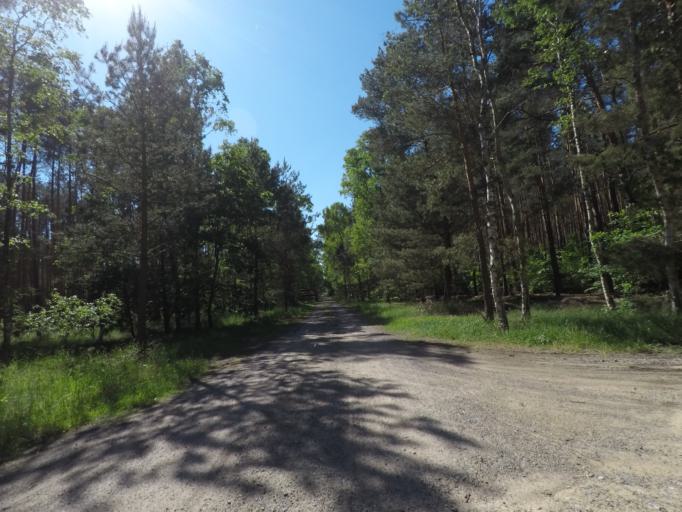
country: DE
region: Brandenburg
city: Melchow
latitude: 52.8275
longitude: 13.7390
